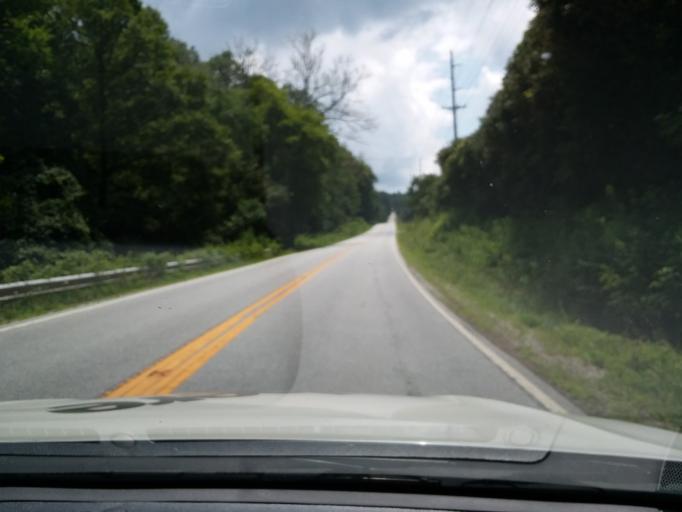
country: US
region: Georgia
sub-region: Rabun County
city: Mountain City
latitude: 35.0228
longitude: -83.3094
